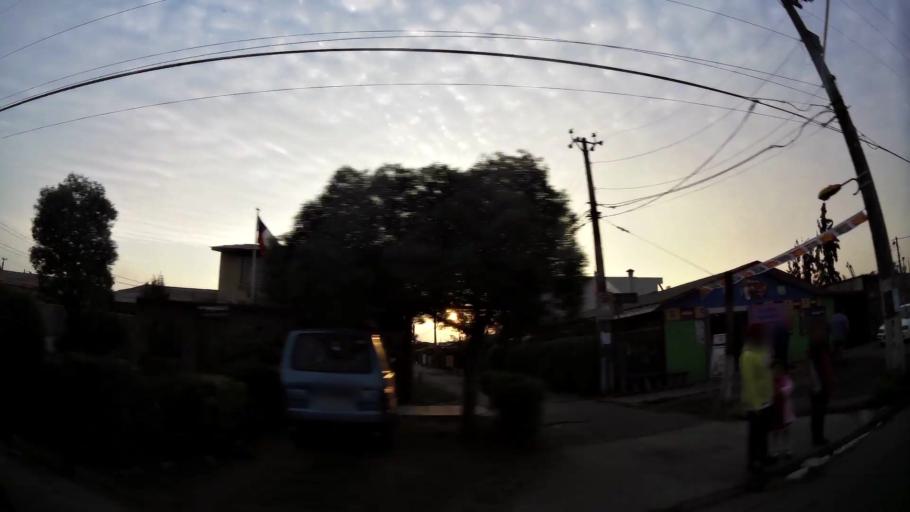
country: CL
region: Santiago Metropolitan
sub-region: Provincia de Santiago
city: Lo Prado
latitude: -33.5149
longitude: -70.7792
